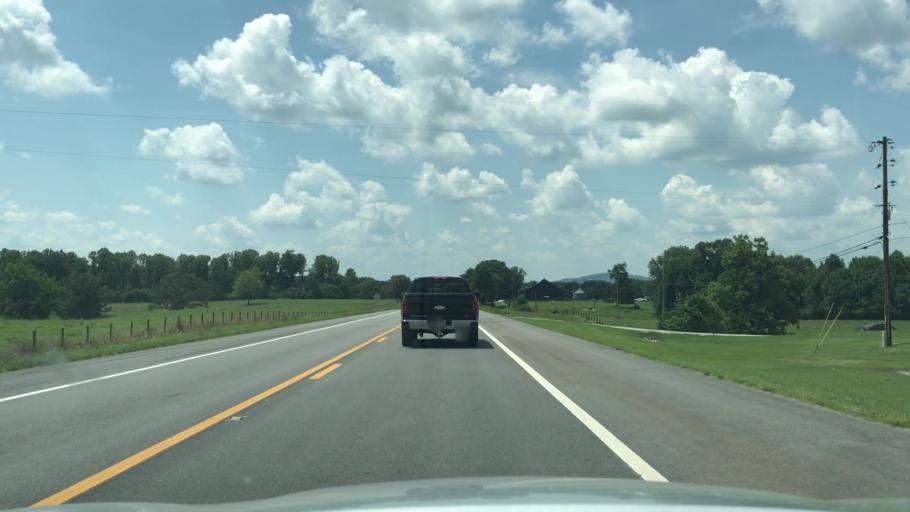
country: US
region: Tennessee
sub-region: Pickett County
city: Byrdstown
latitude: 36.5003
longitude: -85.1774
